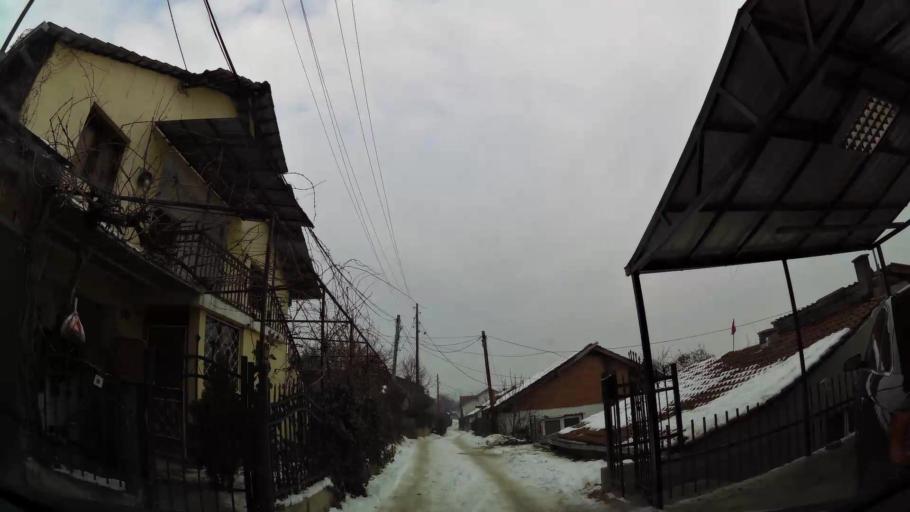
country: MK
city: Kondovo
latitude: 42.0405
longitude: 21.3445
